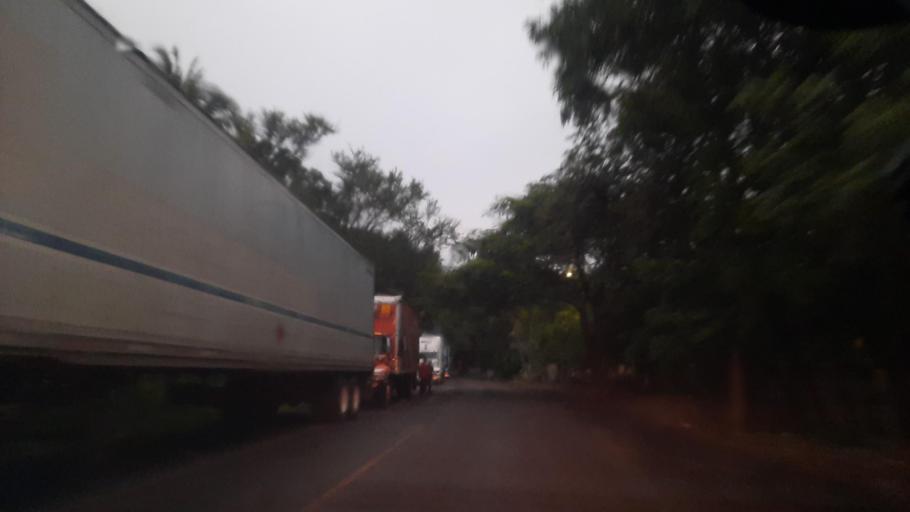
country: GT
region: Jutiapa
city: Atescatempa
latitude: 14.2135
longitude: -89.6836
